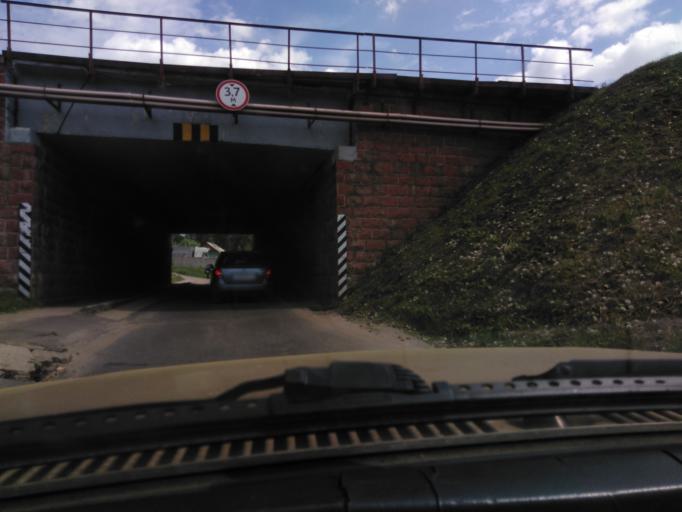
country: BY
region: Mogilev
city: Mahilyow
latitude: 53.9340
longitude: 30.3288
